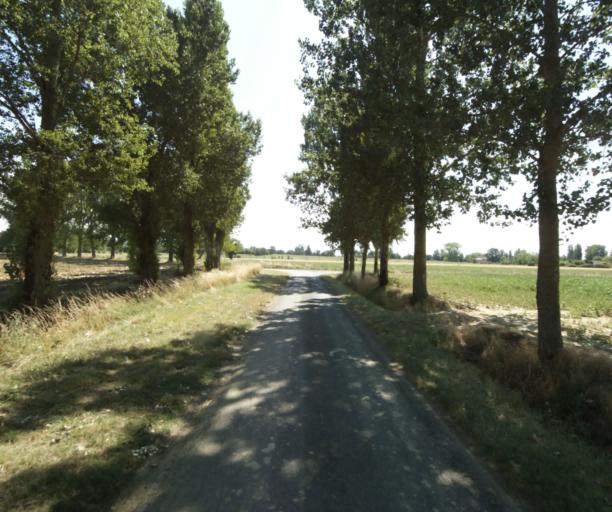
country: FR
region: Midi-Pyrenees
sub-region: Departement de la Haute-Garonne
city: Revel
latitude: 43.4925
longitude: 1.9913
